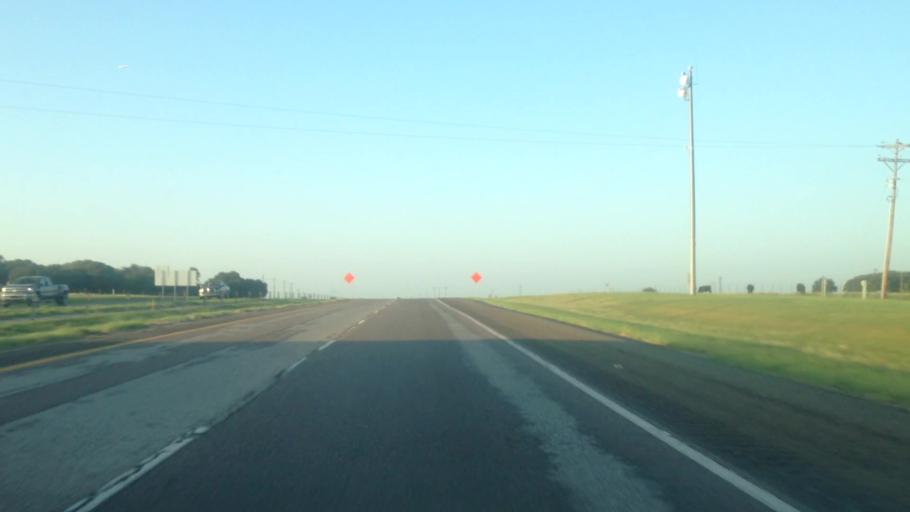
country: US
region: Texas
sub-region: Denton County
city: Argyle
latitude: 33.1450
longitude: -97.1974
